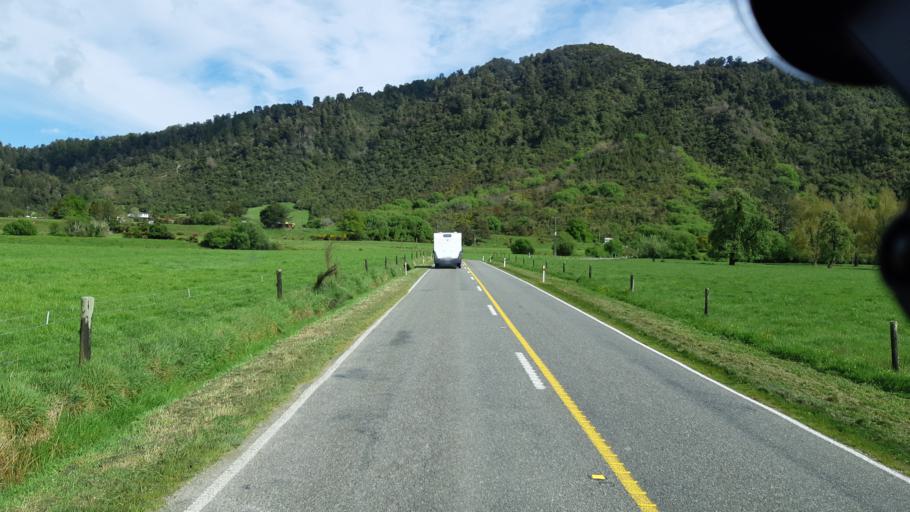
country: NZ
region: West Coast
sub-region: Buller District
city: Westport
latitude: -41.8610
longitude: 171.9416
